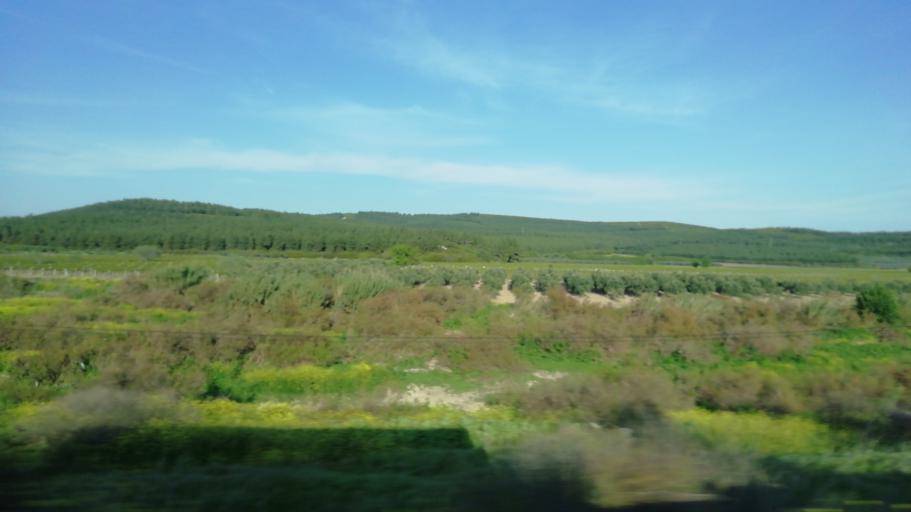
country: TR
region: Manisa
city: Halitpasa
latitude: 38.7847
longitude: 27.6701
